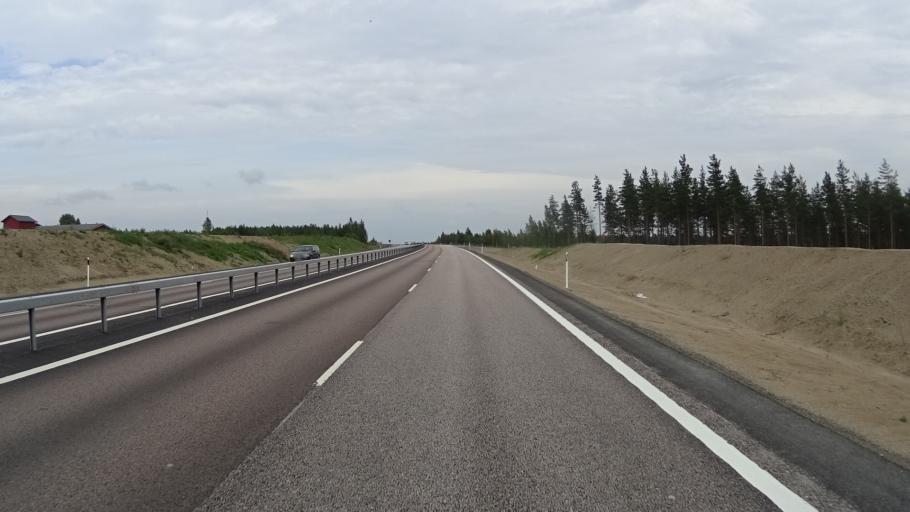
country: FI
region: South Karelia
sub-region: Lappeenranta
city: Lemi
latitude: 60.9876
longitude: 27.9114
